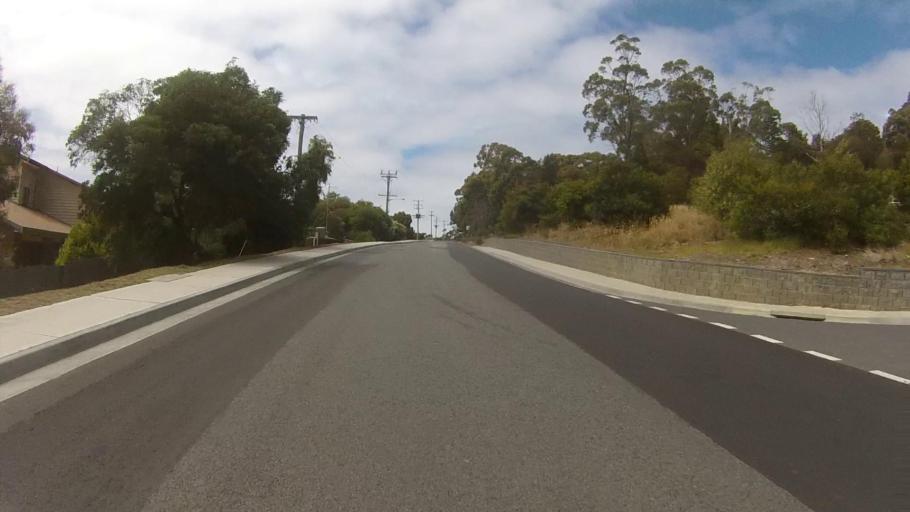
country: AU
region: Tasmania
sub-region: Kingborough
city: Blackmans Bay
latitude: -43.0118
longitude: 147.3208
